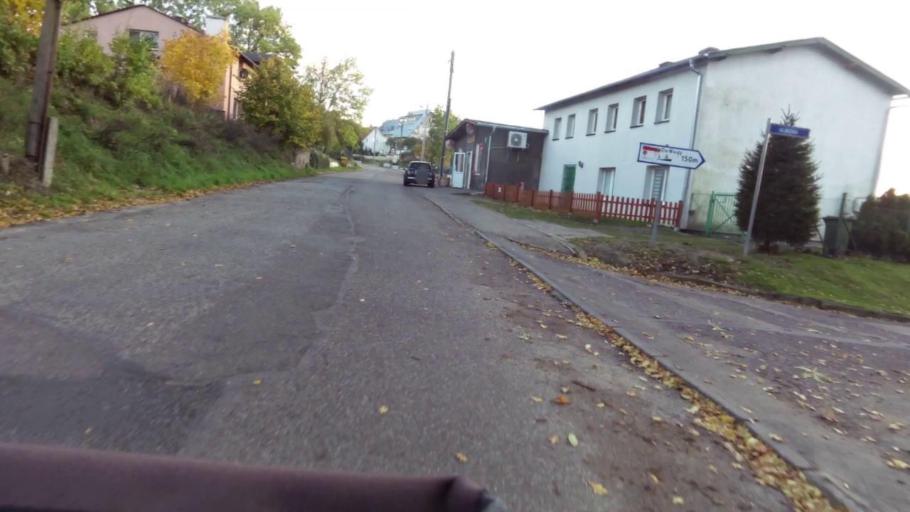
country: PL
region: West Pomeranian Voivodeship
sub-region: Powiat kamienski
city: Miedzyzdroje
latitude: 53.8703
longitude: 14.4276
